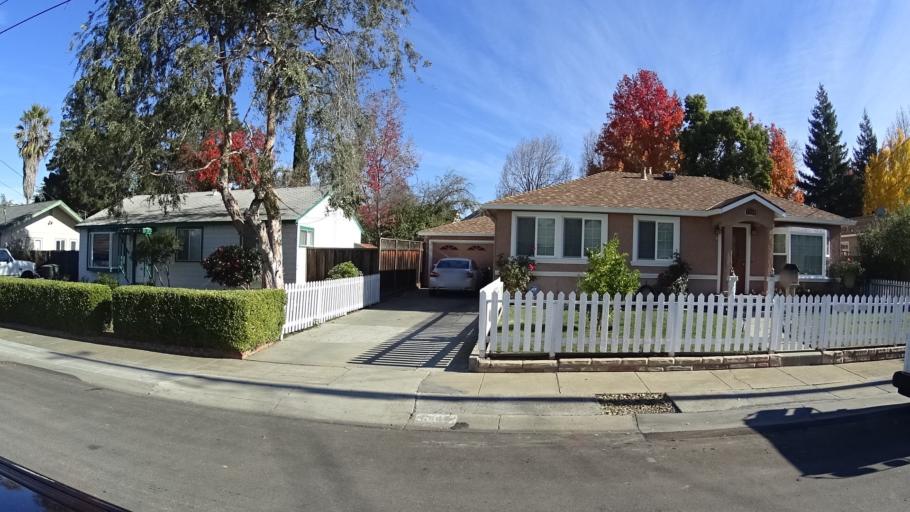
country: US
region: California
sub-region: Santa Clara County
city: Sunnyvale
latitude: 37.3499
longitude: -122.0356
